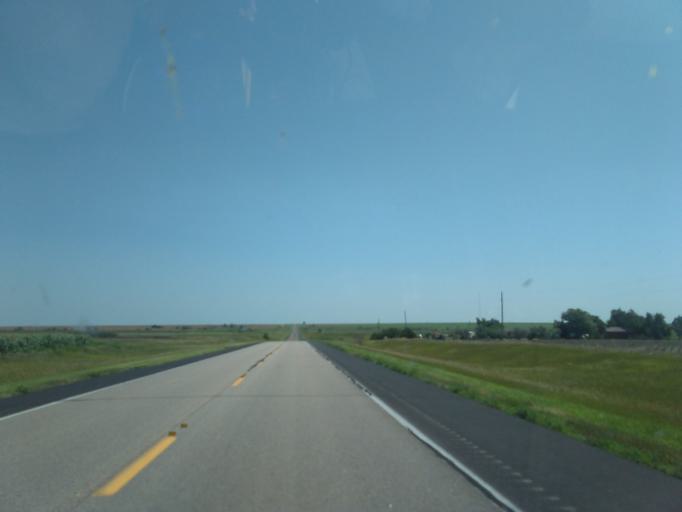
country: US
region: Nebraska
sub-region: Hitchcock County
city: Trenton
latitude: 40.2117
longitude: -100.9542
